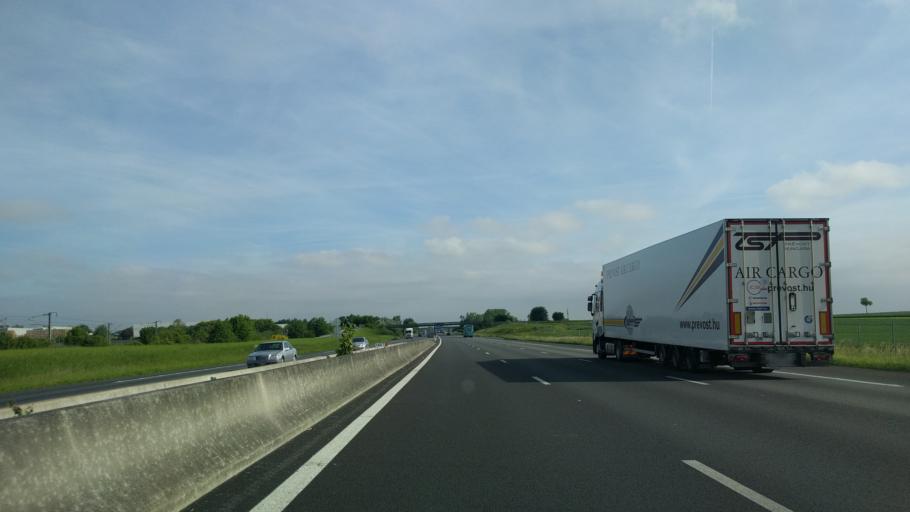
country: FR
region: Nord-Pas-de-Calais
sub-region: Departement du Pas-de-Calais
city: Bapaume
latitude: 50.0940
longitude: 2.8715
